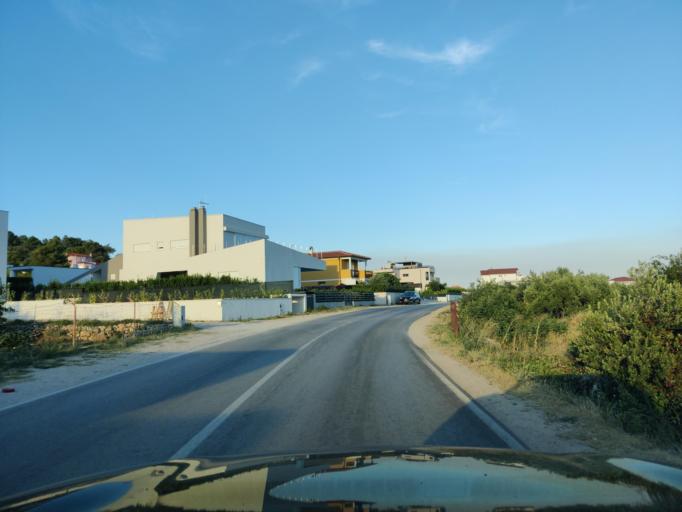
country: HR
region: Sibensko-Kniniska
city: Tribunj
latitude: 43.7589
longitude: 15.7585
